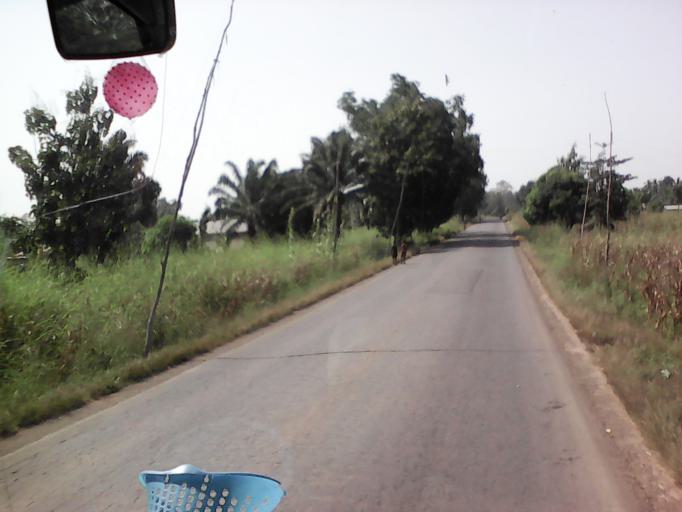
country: TG
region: Centrale
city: Sokode
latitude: 8.8948
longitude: 1.0881
